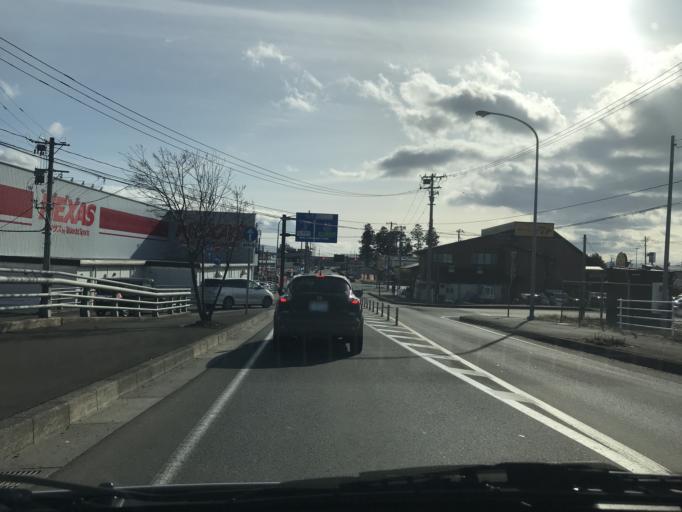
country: JP
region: Iwate
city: Kitakami
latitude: 39.2949
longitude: 141.0978
